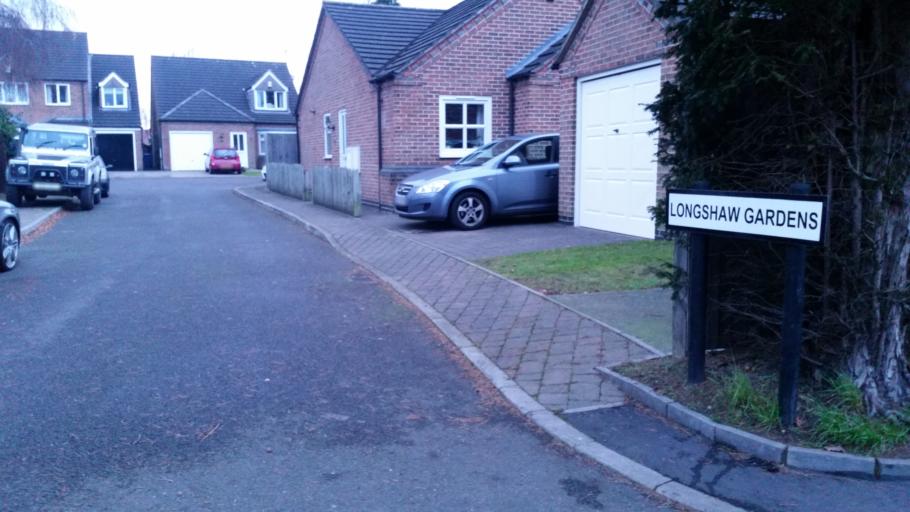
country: GB
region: England
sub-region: Derbyshire
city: Borrowash
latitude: 52.8924
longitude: -1.4305
